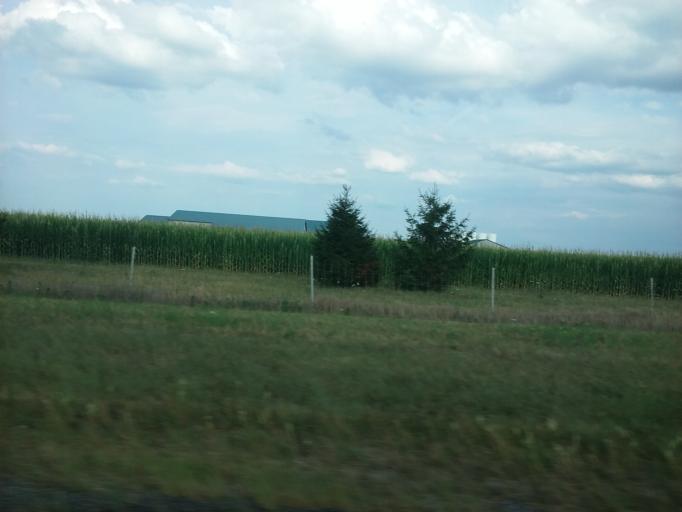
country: US
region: Ohio
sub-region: Wood County
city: Bowling Green
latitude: 41.2811
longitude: -83.6499
